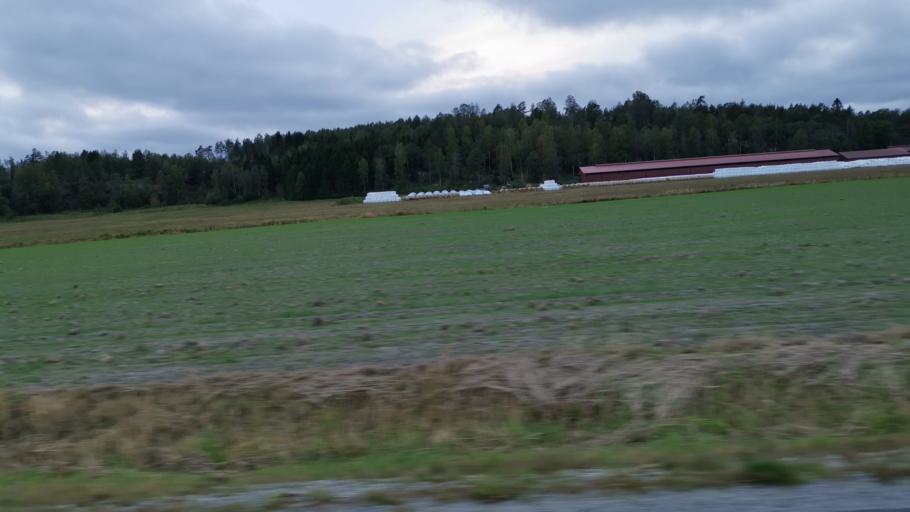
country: SE
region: Vaestra Goetaland
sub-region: Tanums Kommun
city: Tanumshede
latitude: 58.6617
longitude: 11.3467
